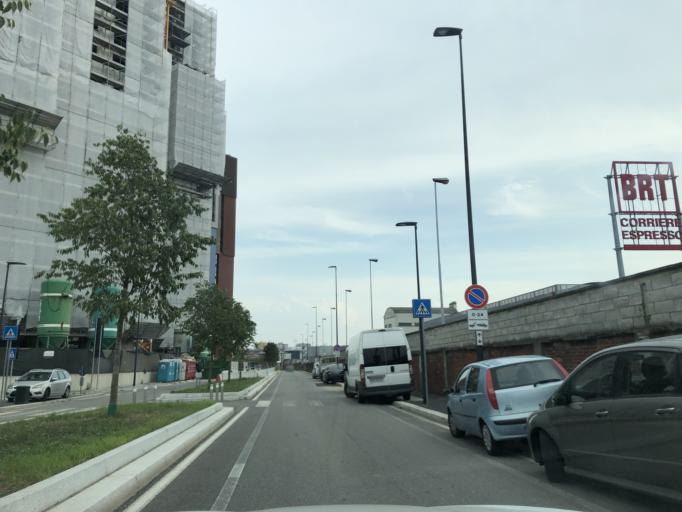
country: IT
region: Lombardy
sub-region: Citta metropolitana di Milano
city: Pero
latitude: 45.5125
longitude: 9.0984
